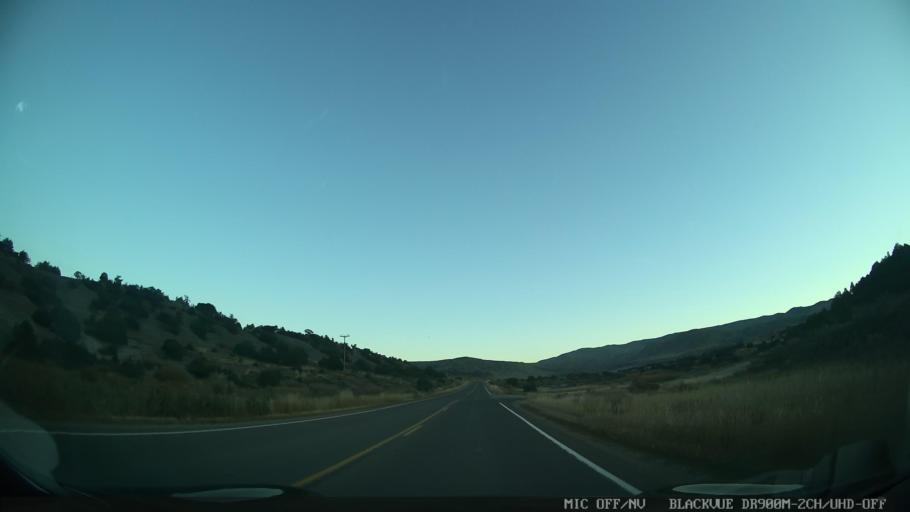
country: US
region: Colorado
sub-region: Eagle County
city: Edwards
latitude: 39.7282
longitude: -106.6785
